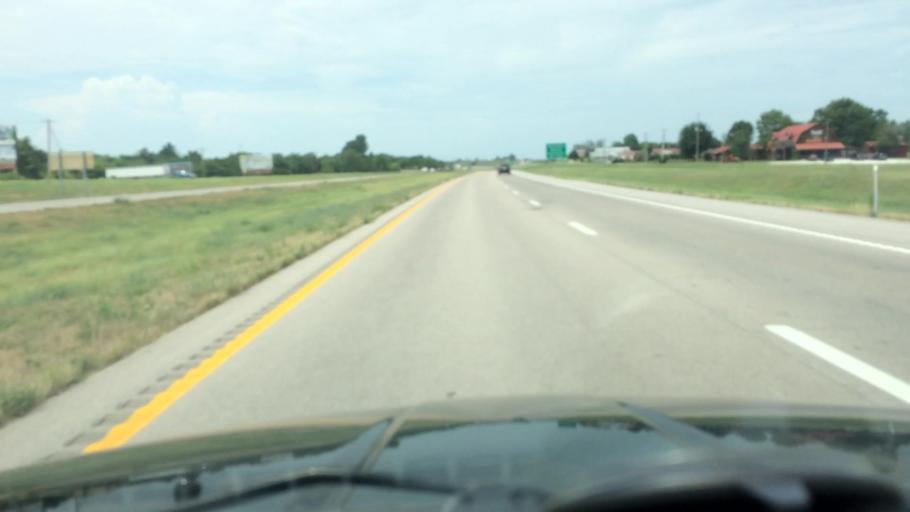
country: US
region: Missouri
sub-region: Polk County
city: Bolivar
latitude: 37.5646
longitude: -93.3936
